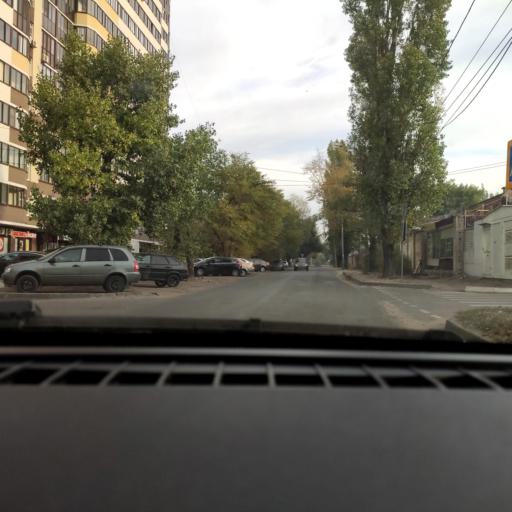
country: RU
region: Voronezj
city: Maslovka
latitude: 51.6357
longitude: 39.2727
